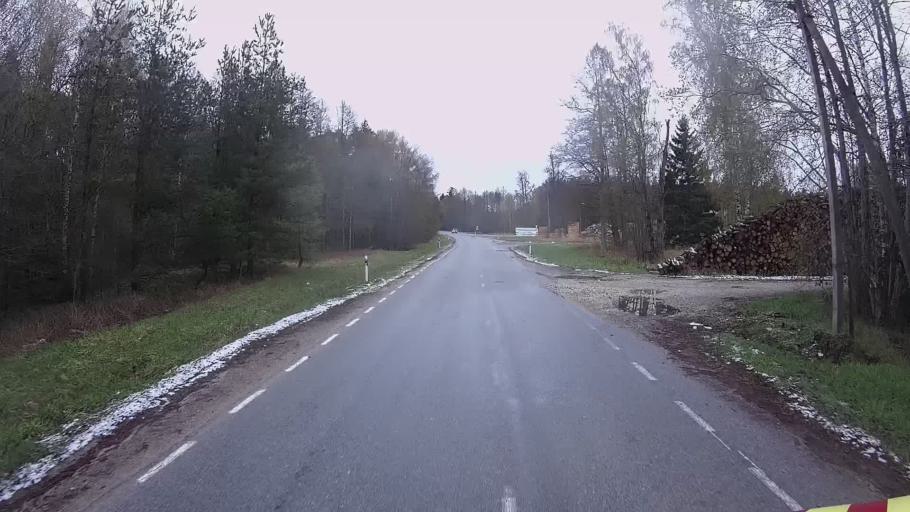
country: EE
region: Hiiumaa
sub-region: Kaerdla linn
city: Kardla
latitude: 59.0703
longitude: 22.6897
